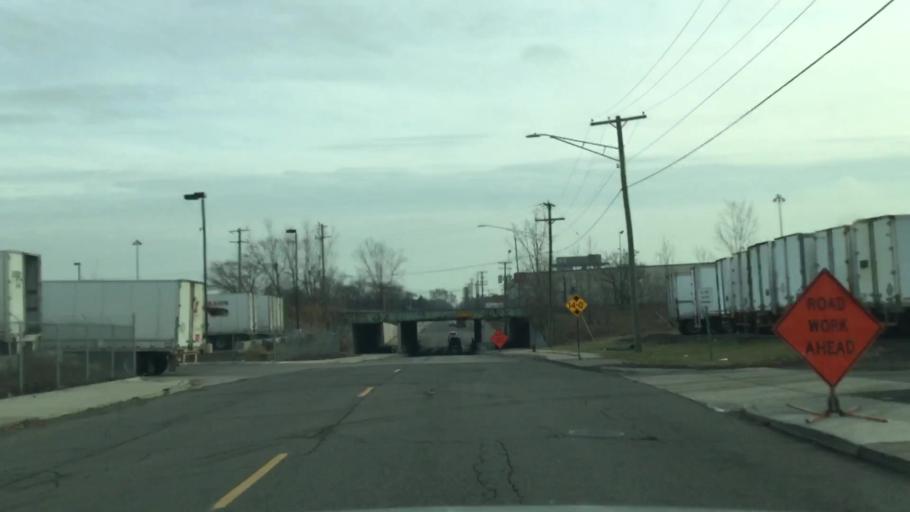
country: US
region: Michigan
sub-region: Wayne County
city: Detroit
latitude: 42.3273
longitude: -83.1009
